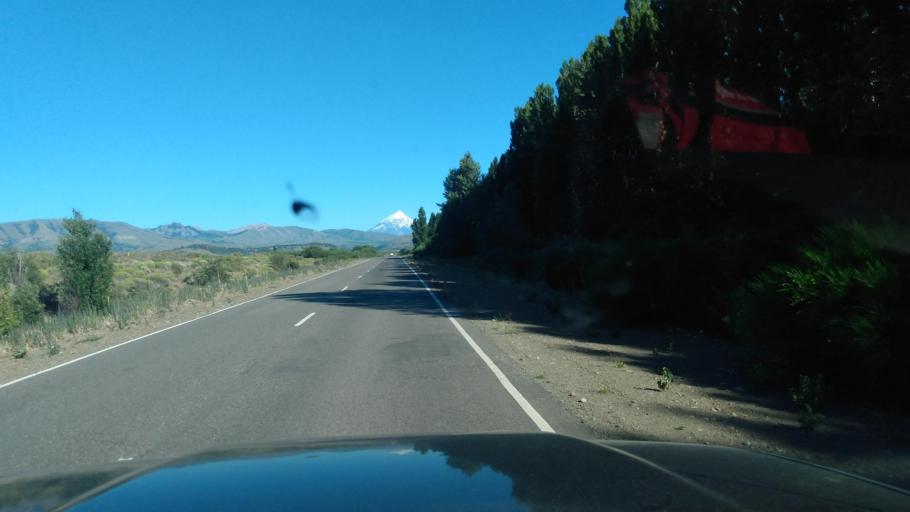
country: AR
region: Neuquen
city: Junin de los Andes
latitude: -39.8977
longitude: -71.1433
